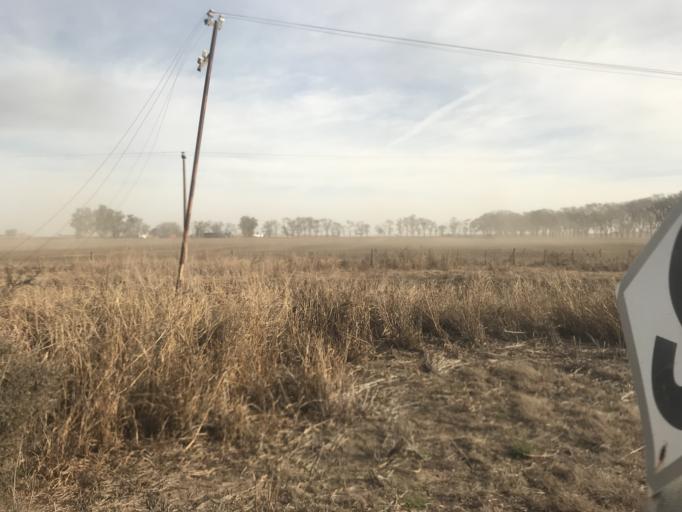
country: AR
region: Cordoba
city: Laguna Larga
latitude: -31.7437
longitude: -63.8322
